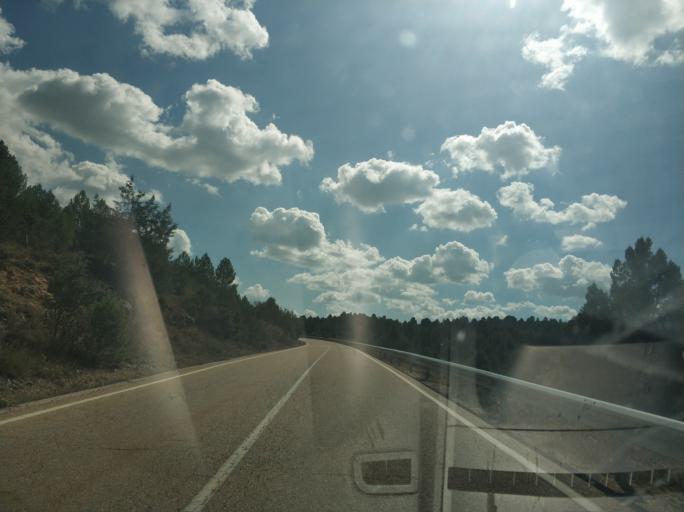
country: ES
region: Castille and Leon
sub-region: Provincia de Soria
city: Casarejos
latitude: 41.7842
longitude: -3.0329
